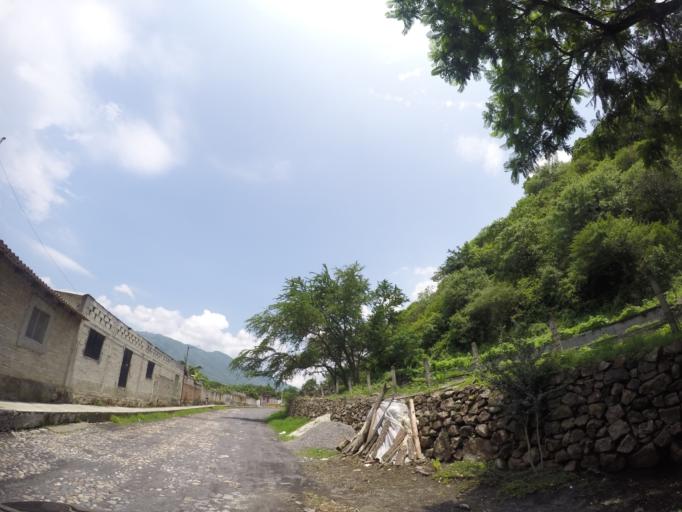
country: MX
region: Nayarit
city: Jala
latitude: 21.1065
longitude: -104.4392
